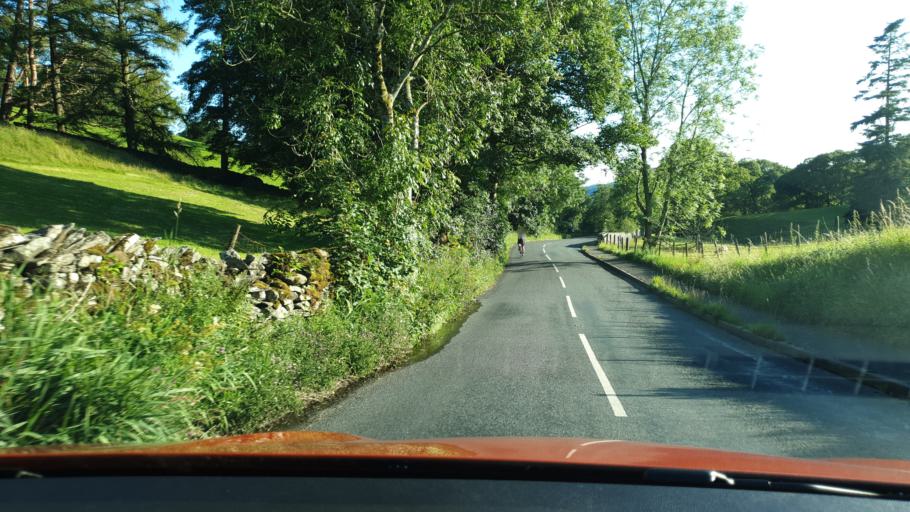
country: GB
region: England
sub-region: Cumbria
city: Windermere
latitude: 54.4066
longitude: -2.9096
